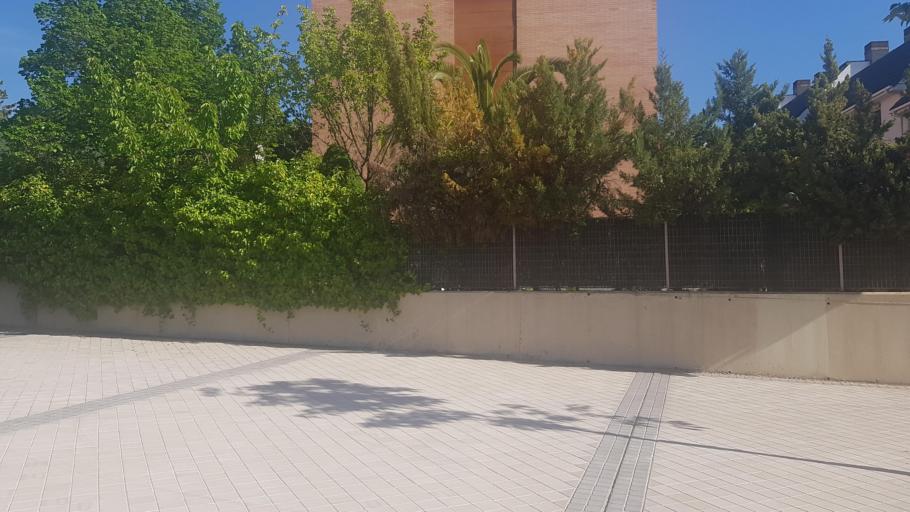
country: ES
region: Madrid
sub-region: Provincia de Madrid
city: Pozuelo de Alarcon
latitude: 40.4541
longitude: -3.7777
